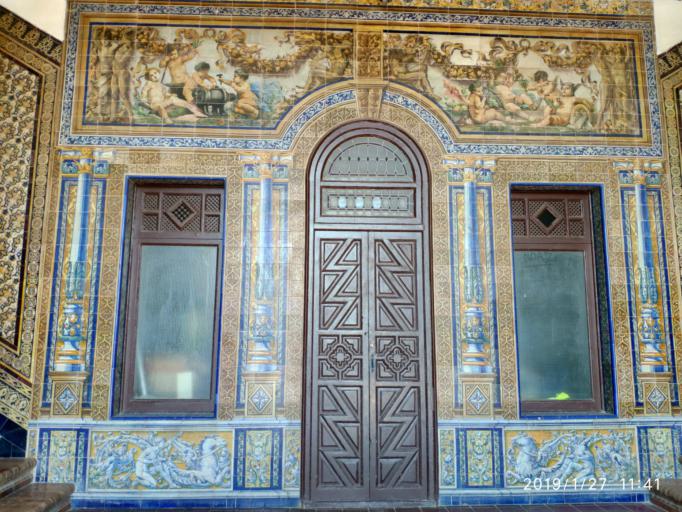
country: ES
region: Andalusia
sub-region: Provincia de Sevilla
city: Sevilla
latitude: 37.3762
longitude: -5.9857
